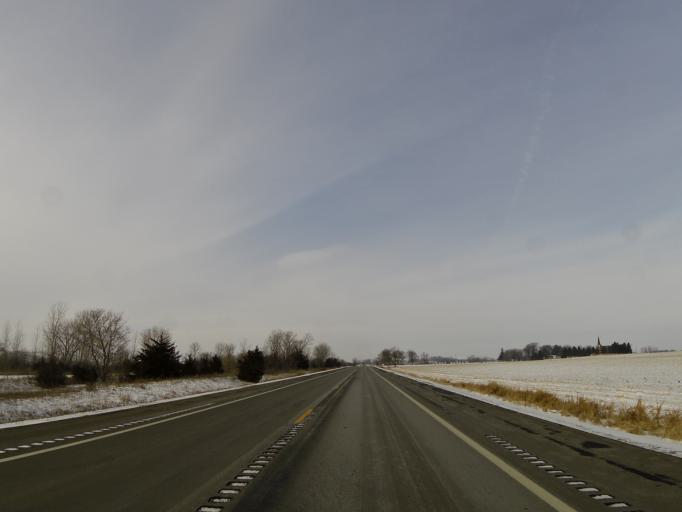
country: US
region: Minnesota
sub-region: McLeod County
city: Hutchinson
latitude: 44.9146
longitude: -94.4562
